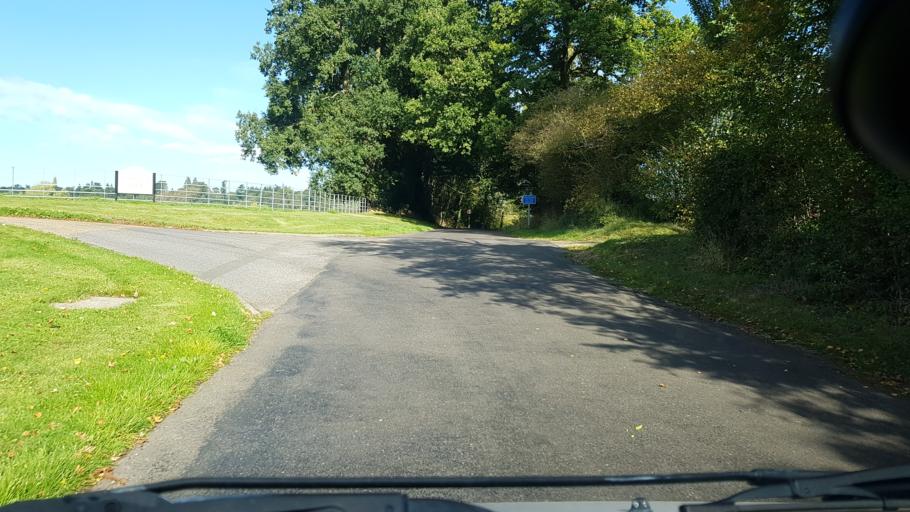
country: GB
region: England
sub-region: Surrey
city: Shalford
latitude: 51.2131
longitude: -0.5961
